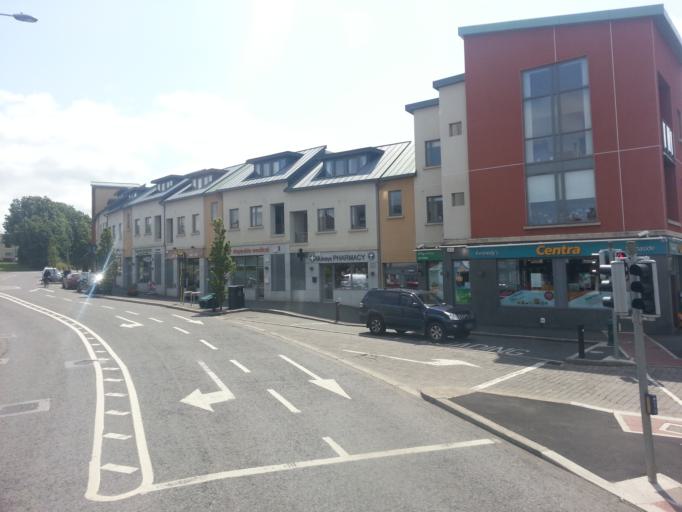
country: IE
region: Leinster
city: Sandyford
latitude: 53.2530
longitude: -6.2142
